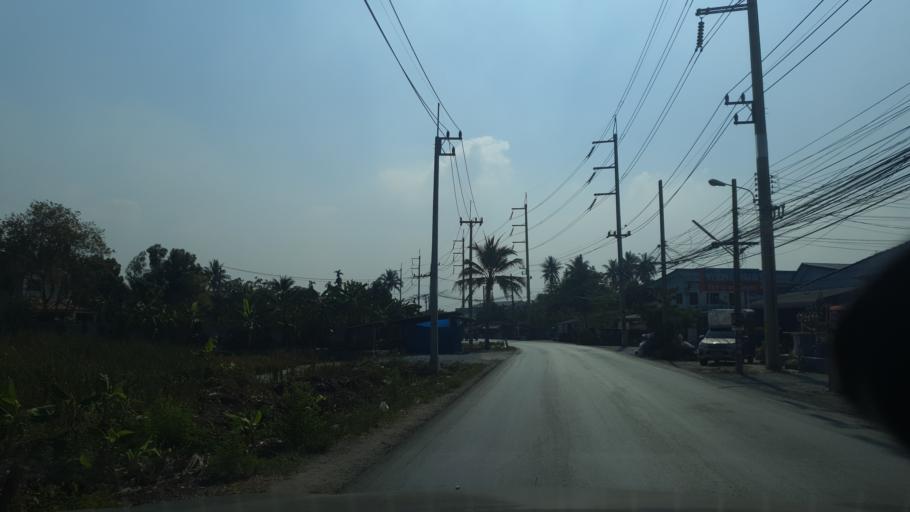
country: TH
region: Nakhon Pathom
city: Salaya
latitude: 13.7762
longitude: 100.2765
